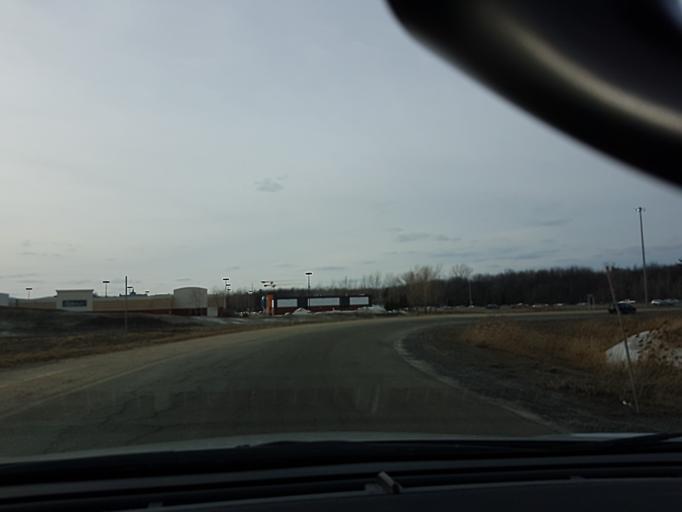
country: CA
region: Quebec
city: L'Ancienne-Lorette
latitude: 46.7820
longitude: -71.3430
